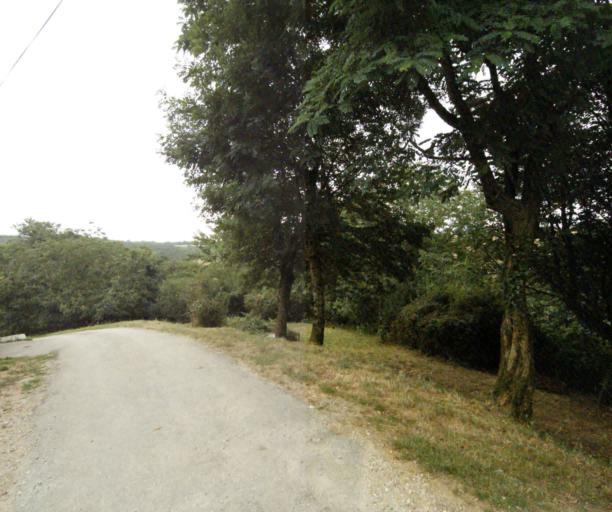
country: FR
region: Midi-Pyrenees
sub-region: Departement du Tarn
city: Soreze
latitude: 43.3920
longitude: 2.0561
